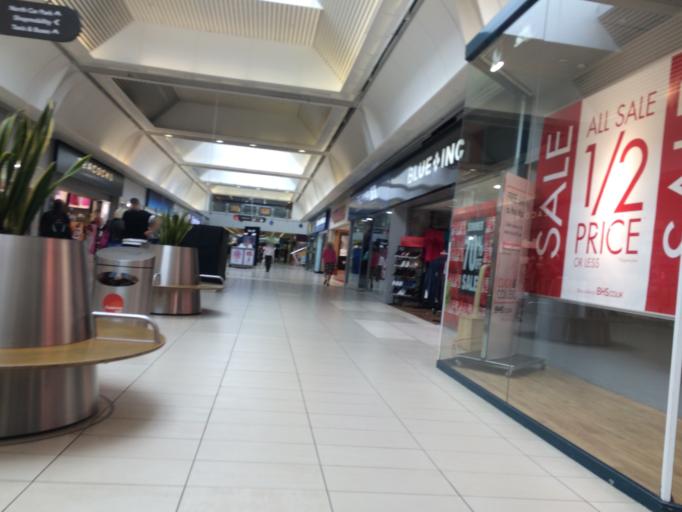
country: GB
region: Scotland
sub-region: Edinburgh
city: Edinburgh
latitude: 55.9260
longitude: -3.1643
